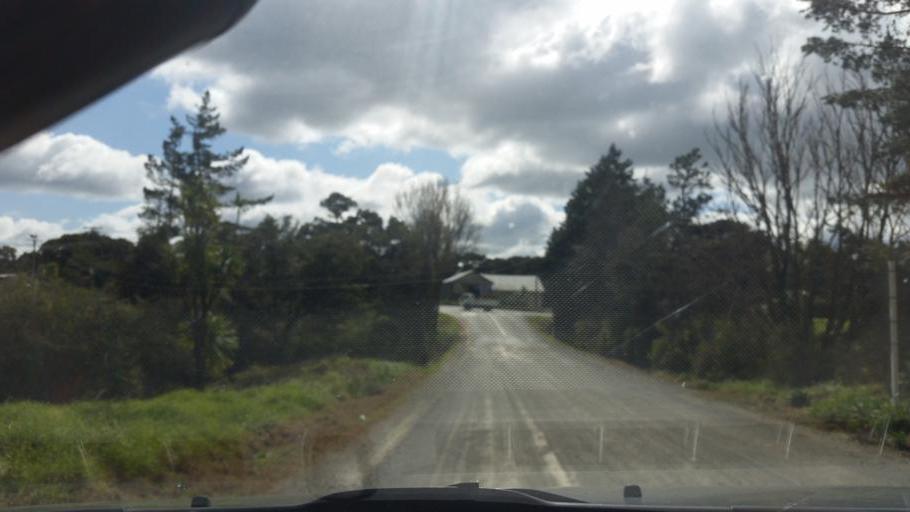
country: NZ
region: Auckland
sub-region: Auckland
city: Wellsford
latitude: -36.1397
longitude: 174.5094
